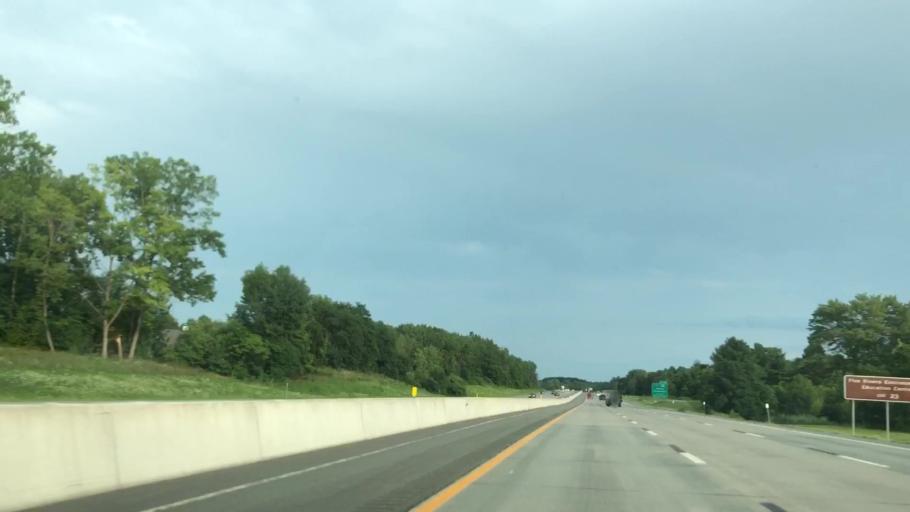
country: US
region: New York
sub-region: Albany County
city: Delmar
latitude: 42.6483
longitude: -73.8157
